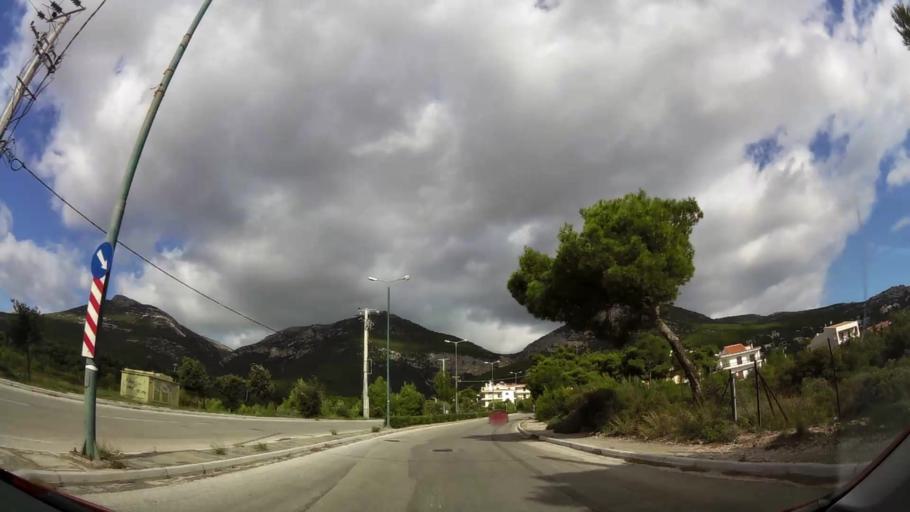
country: GR
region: Attica
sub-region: Nomarchia Anatolikis Attikis
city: Thrakomakedones
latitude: 38.1357
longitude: 23.7512
